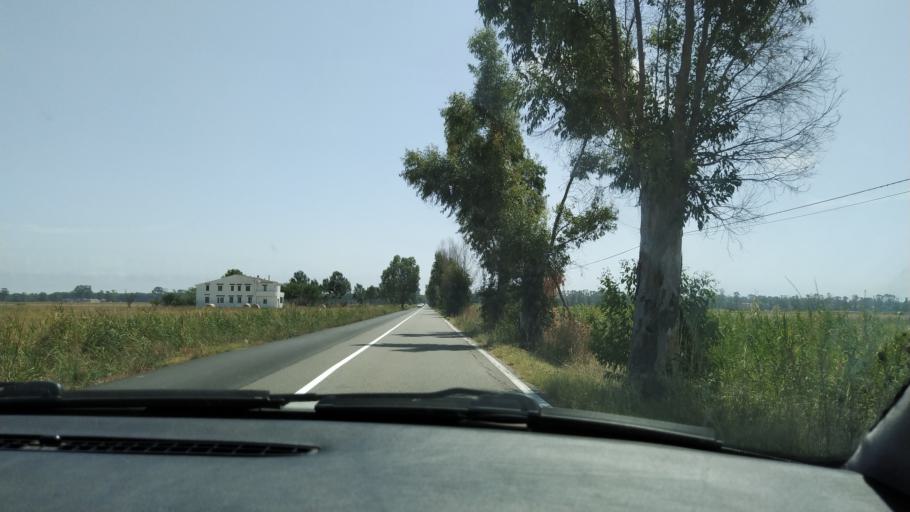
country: IT
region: Basilicate
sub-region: Provincia di Matera
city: Marconia
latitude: 40.3303
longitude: 16.7826
